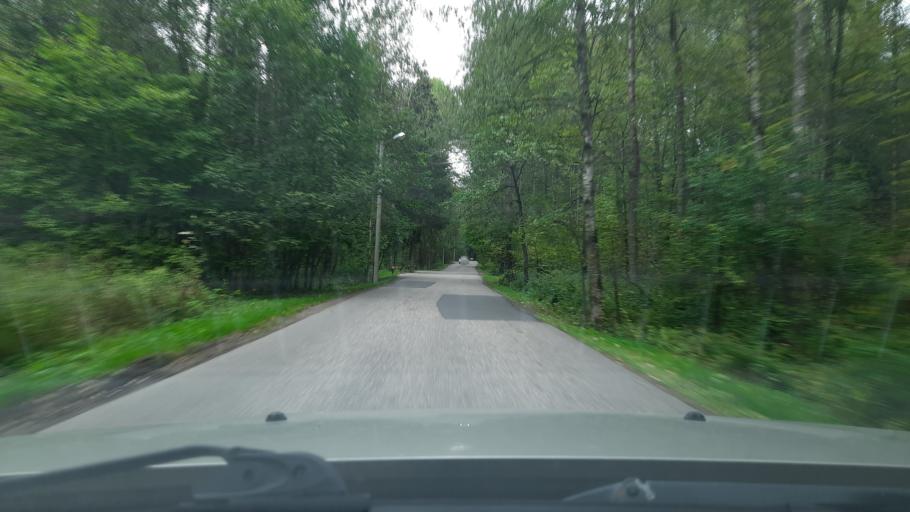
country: RU
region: Moskovskaya
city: Odintsovo
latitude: 55.7077
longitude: 37.2999
